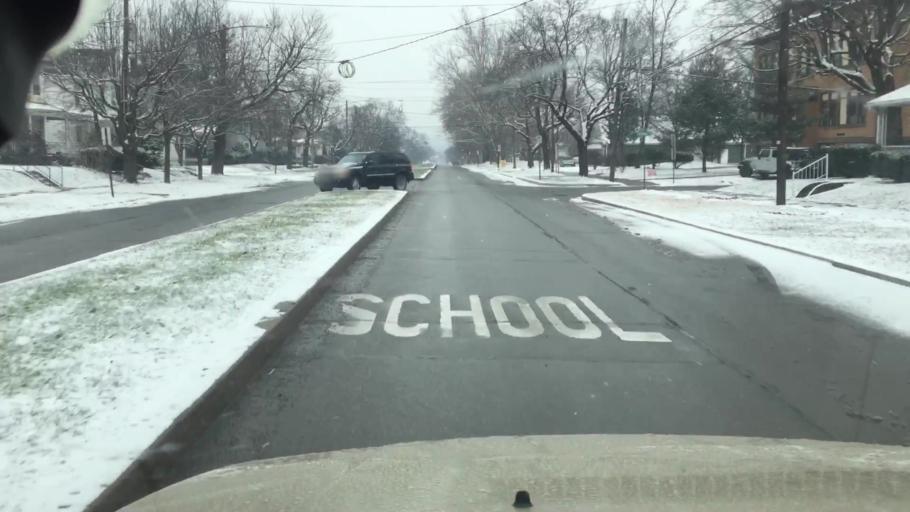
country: US
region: Pennsylvania
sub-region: Columbia County
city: Berwick
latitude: 41.0649
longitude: -76.2423
